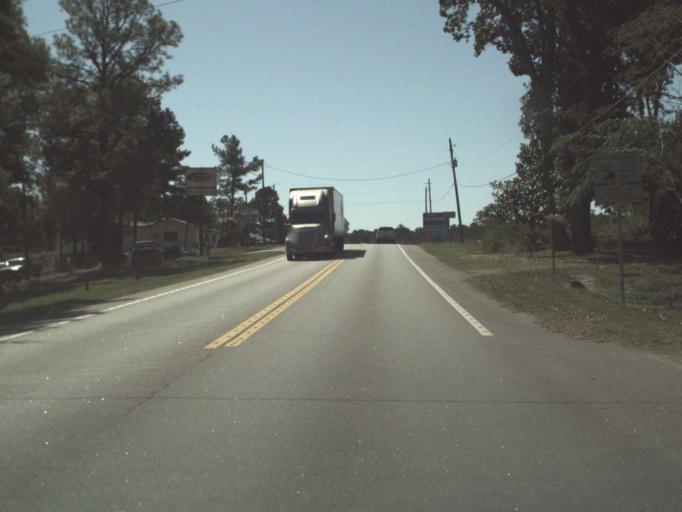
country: US
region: Alabama
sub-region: Covington County
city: Florala
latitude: 30.9939
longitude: -86.3343
